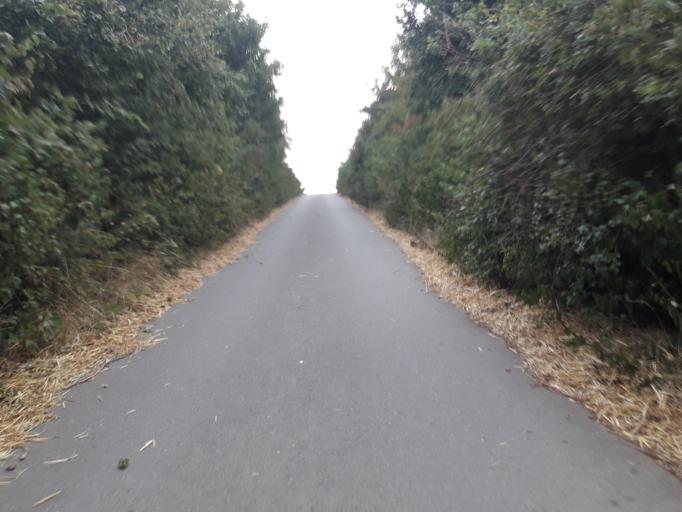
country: DE
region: North Rhine-Westphalia
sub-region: Regierungsbezirk Detmold
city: Paderborn
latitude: 51.6820
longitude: 8.7232
